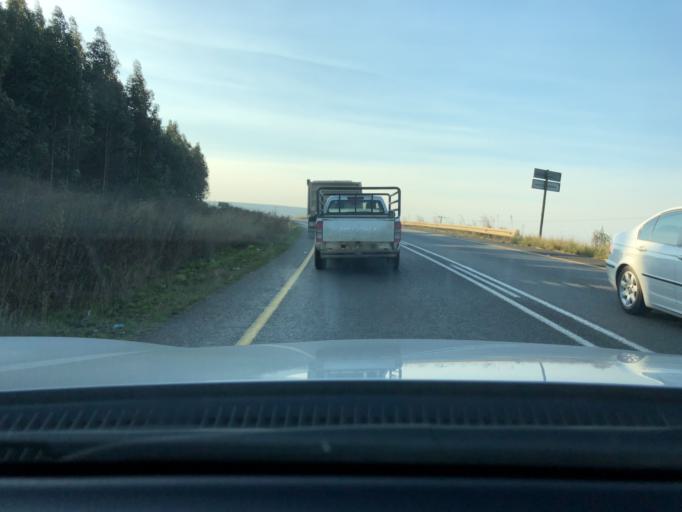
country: ZA
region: KwaZulu-Natal
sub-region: Sisonke District Municipality
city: Ixopo
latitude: -30.2345
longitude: 30.1418
